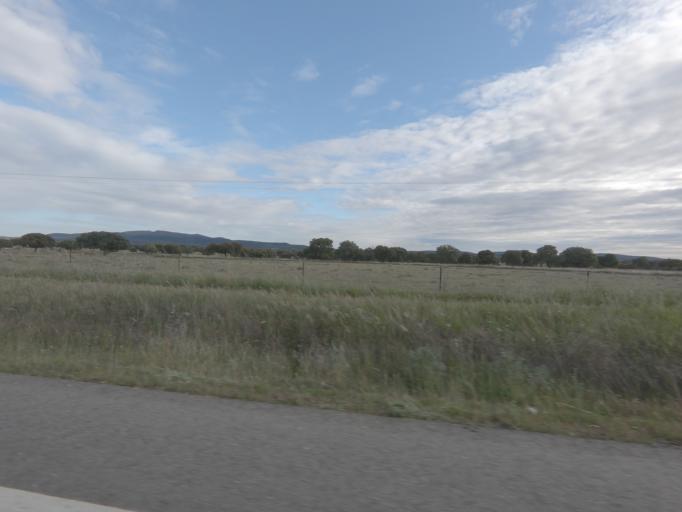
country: ES
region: Extremadura
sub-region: Provincia de Caceres
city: Torrejoncillo
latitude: 39.8829
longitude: -6.4631
